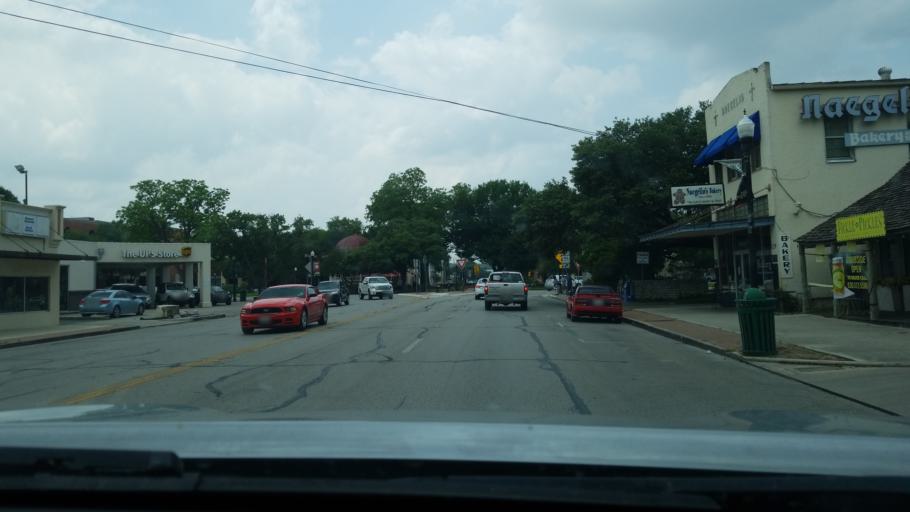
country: US
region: Texas
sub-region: Comal County
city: New Braunfels
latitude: 29.7024
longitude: -98.1238
